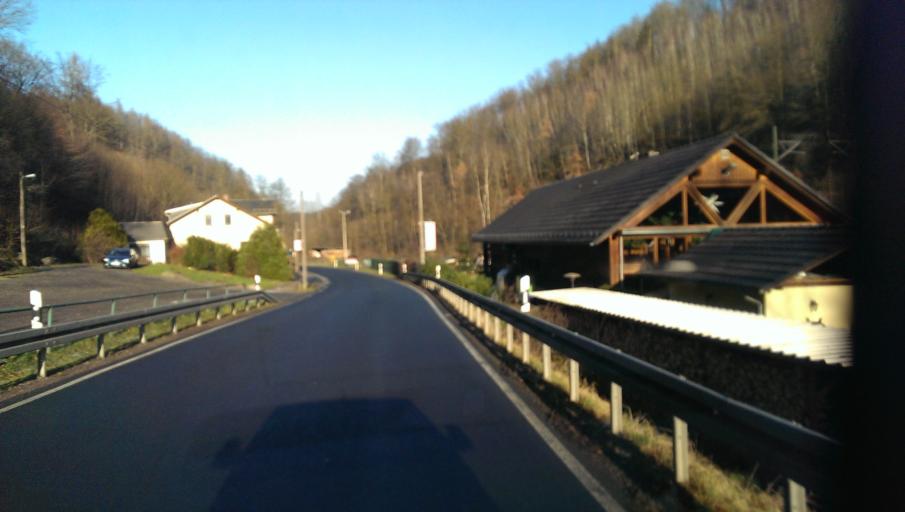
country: DE
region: Saxony
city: Tharandt
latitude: 50.9579
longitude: 13.5809
